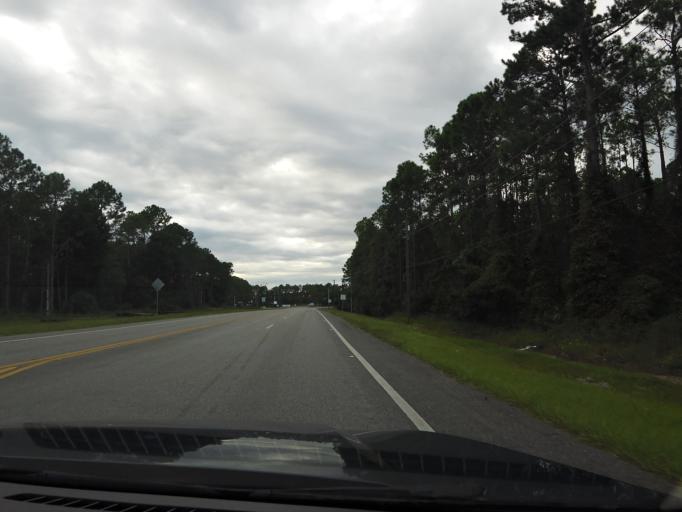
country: US
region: Florida
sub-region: Flagler County
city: Bunnell
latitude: 29.4971
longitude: -81.2622
